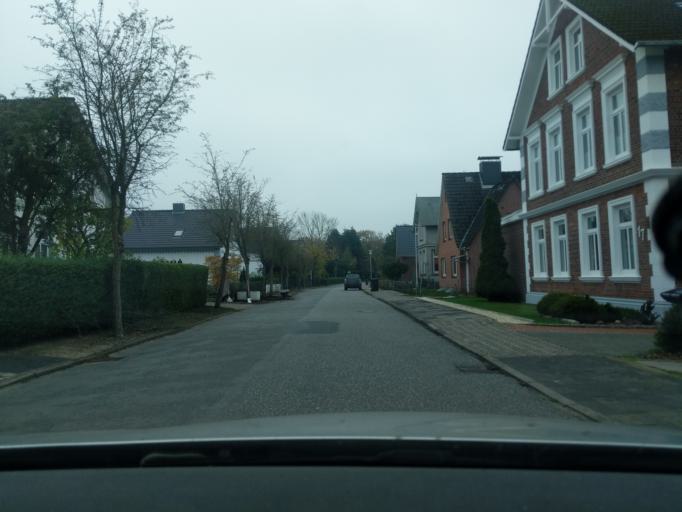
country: DE
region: Lower Saxony
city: Wanna
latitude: 53.8263
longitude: 8.7758
